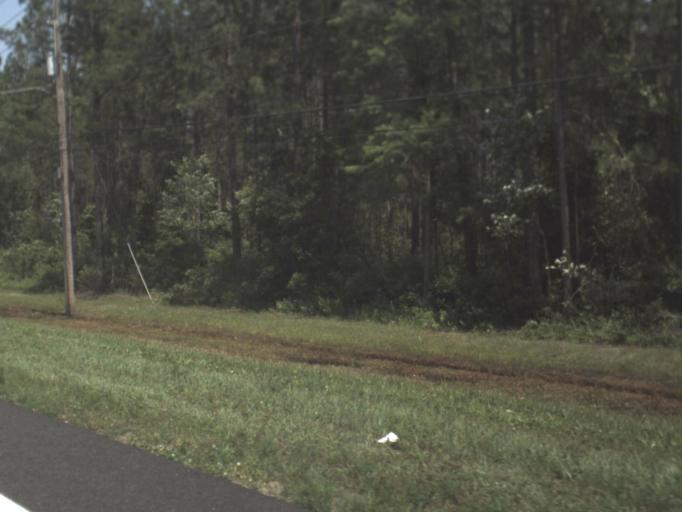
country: US
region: Florida
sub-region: Duval County
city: Baldwin
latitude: 30.2506
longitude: -81.8827
